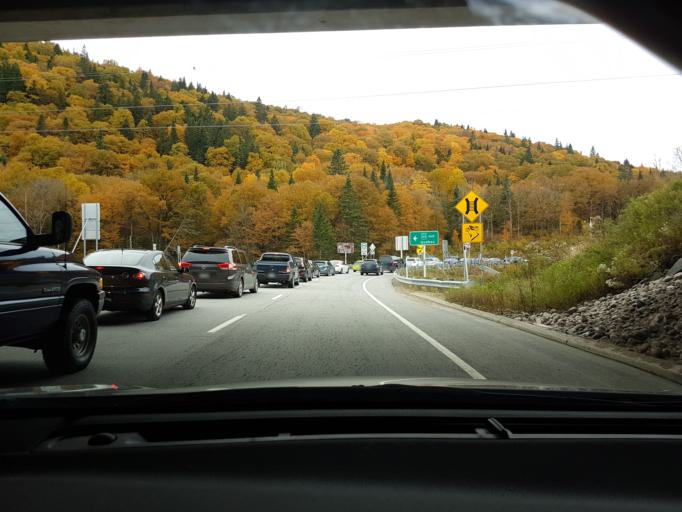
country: CA
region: Quebec
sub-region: Capitale-Nationale
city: Shannon
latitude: 47.1069
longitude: -71.3450
